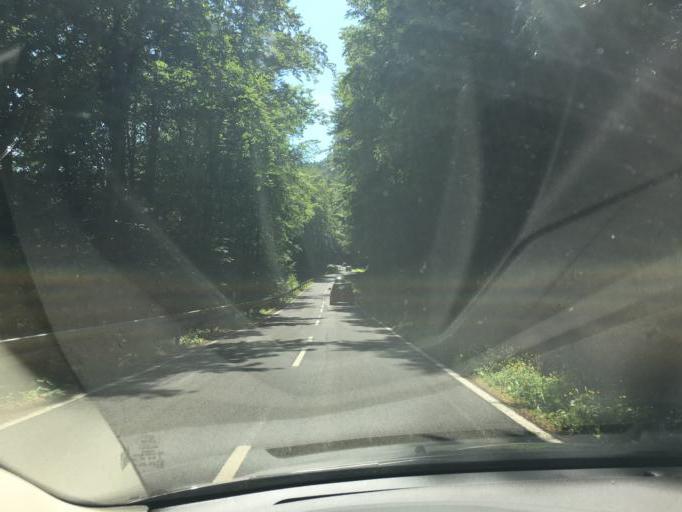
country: DE
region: Hesse
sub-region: Regierungsbezirk Kassel
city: Malsfeld
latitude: 51.0748
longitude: 9.5458
